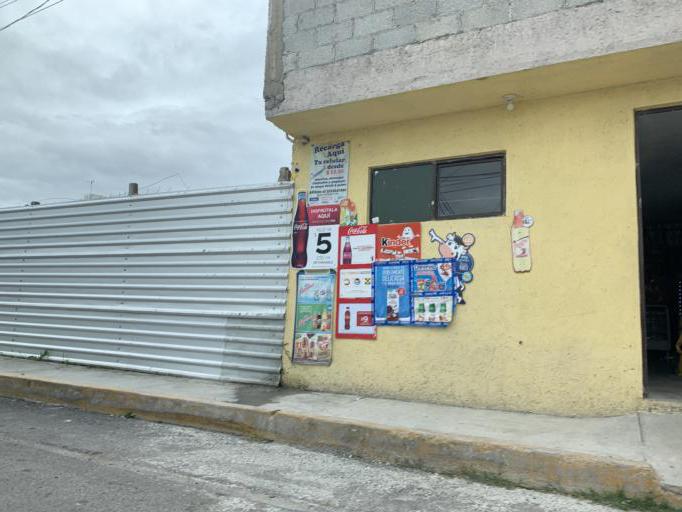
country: MX
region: Puebla
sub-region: Puebla
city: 18 de Marzo
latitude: 18.9811
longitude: -98.1945
